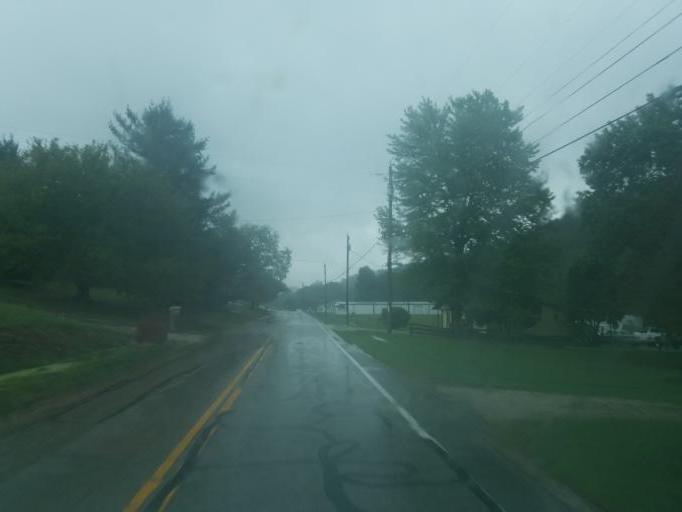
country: US
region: Kentucky
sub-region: Carter County
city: Olive Hill
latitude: 38.2900
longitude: -83.2921
